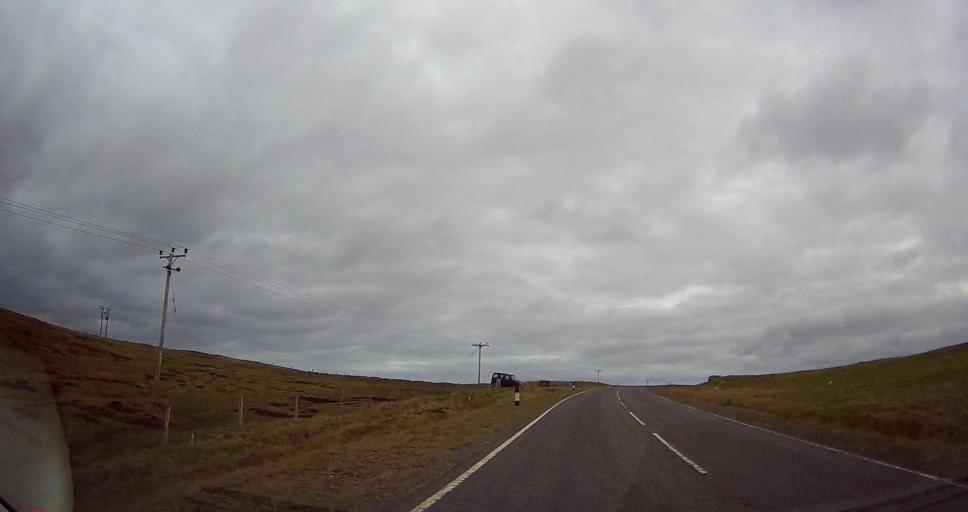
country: GB
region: Scotland
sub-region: Shetland Islands
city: Shetland
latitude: 60.6534
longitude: -1.0674
